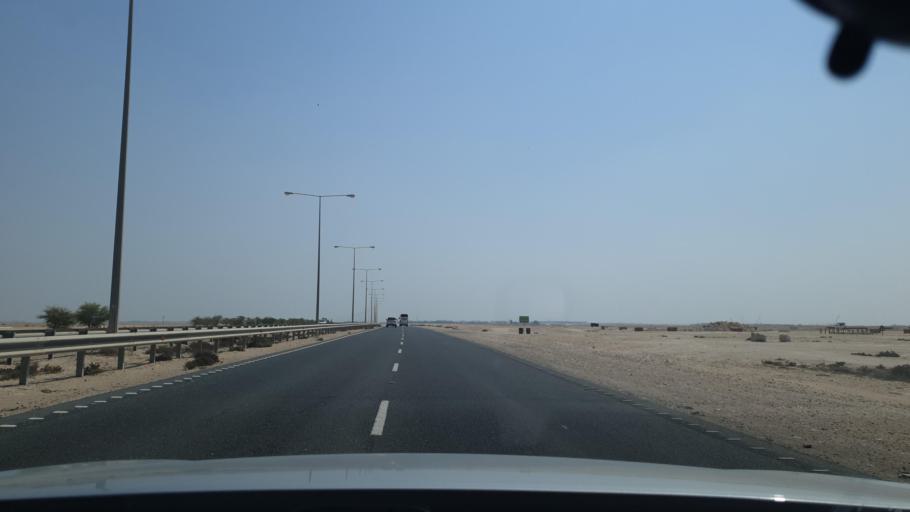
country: QA
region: Al Khawr
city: Al Khawr
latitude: 25.7489
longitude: 51.4791
